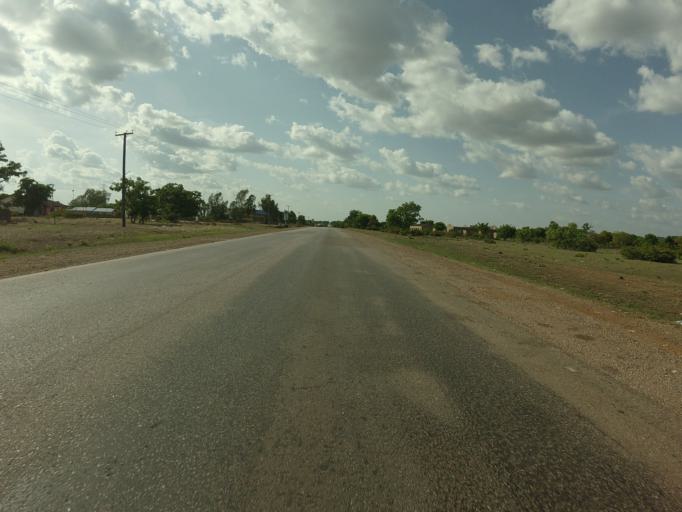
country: GH
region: Upper East
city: Bolgatanga
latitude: 10.6488
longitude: -0.8576
